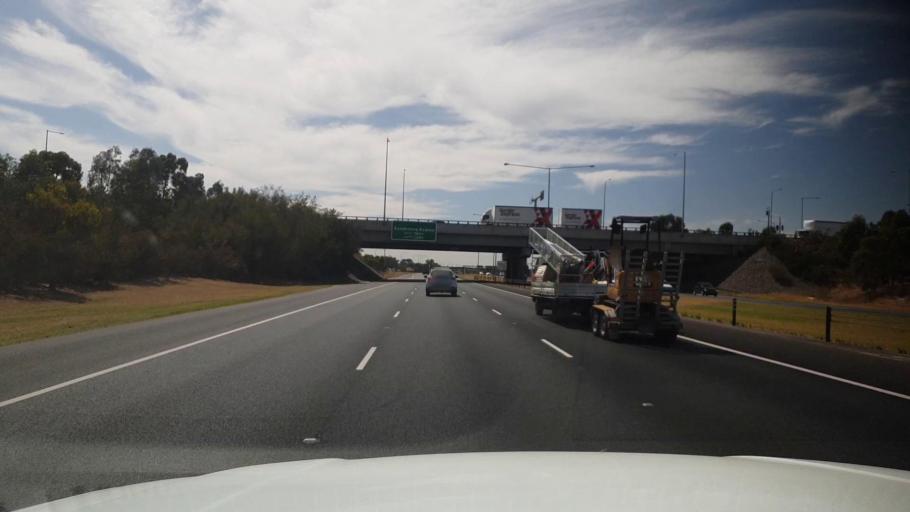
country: AU
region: Victoria
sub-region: Greater Dandenong
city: Keysborough
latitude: -38.0124
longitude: 145.1881
